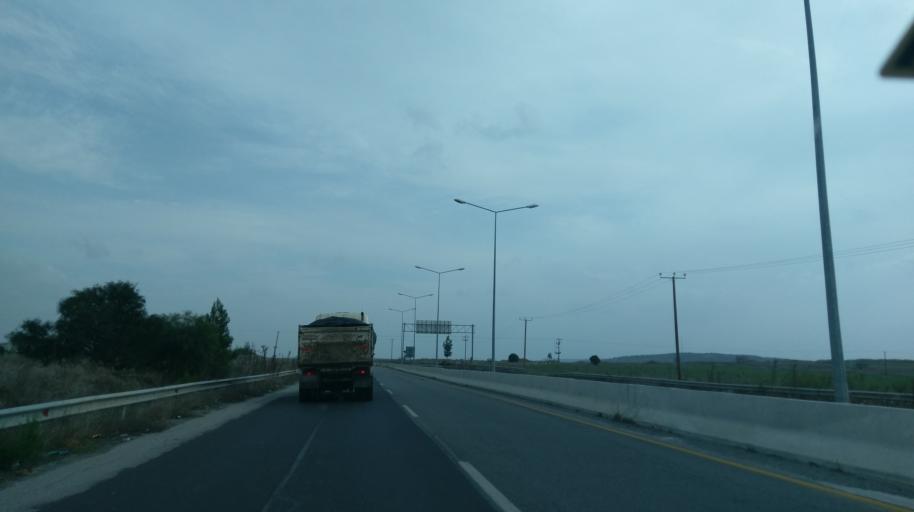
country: CY
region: Lefkosia
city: Mammari
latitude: 35.2160
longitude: 33.1819
